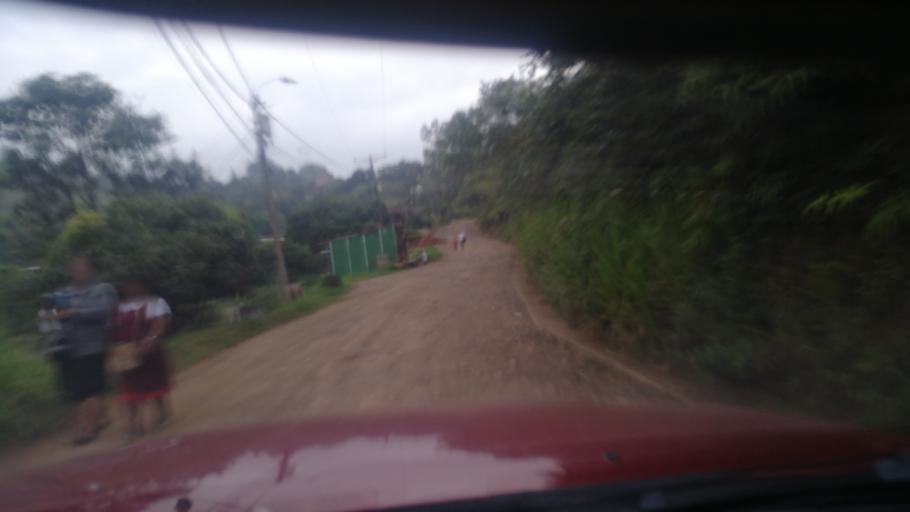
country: CO
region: Valle del Cauca
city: Cali
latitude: 3.4994
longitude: -76.5492
